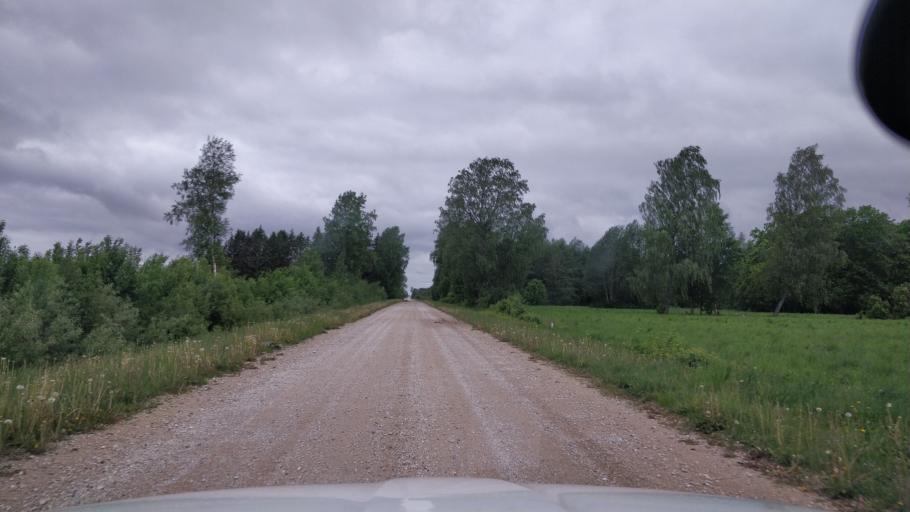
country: EE
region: Raplamaa
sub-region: Maerjamaa vald
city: Marjamaa
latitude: 58.7163
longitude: 24.2735
